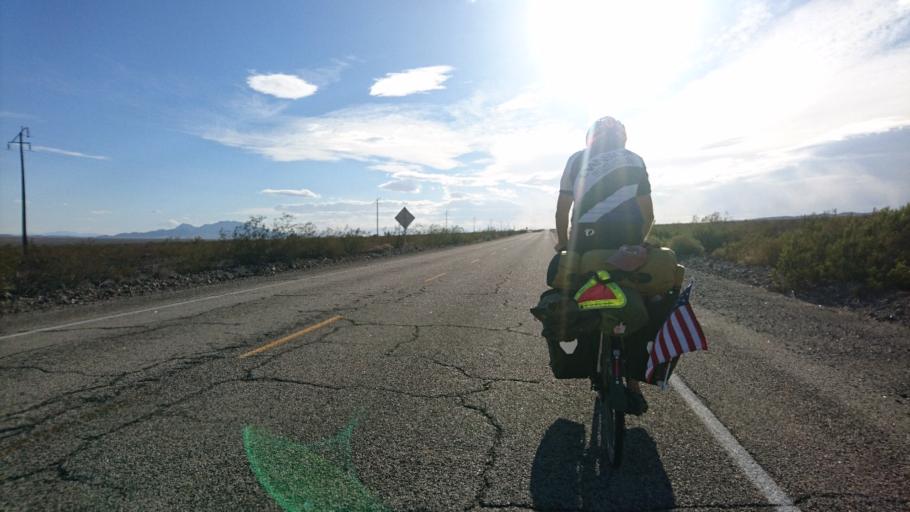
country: US
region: California
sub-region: San Bernardino County
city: Needles
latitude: 34.6841
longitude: -115.3210
